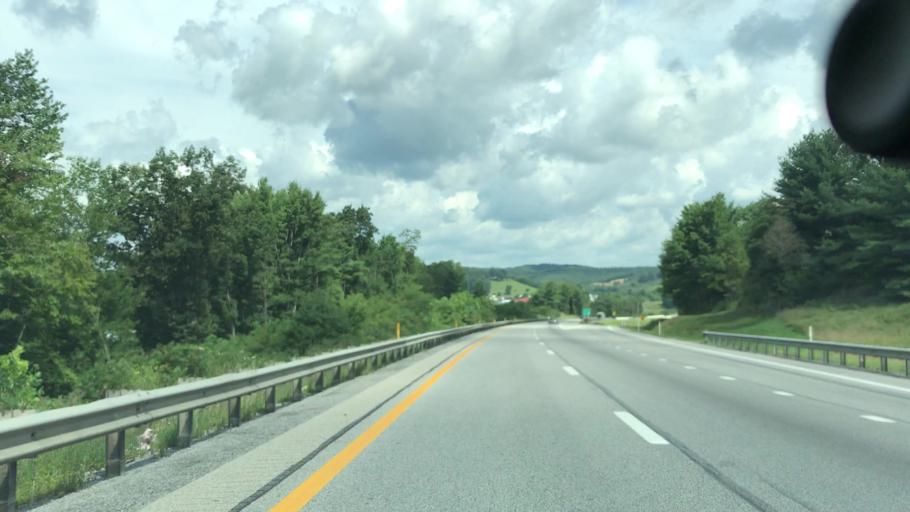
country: US
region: West Virginia
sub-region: Mercer County
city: Athens
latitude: 37.4192
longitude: -81.0648
